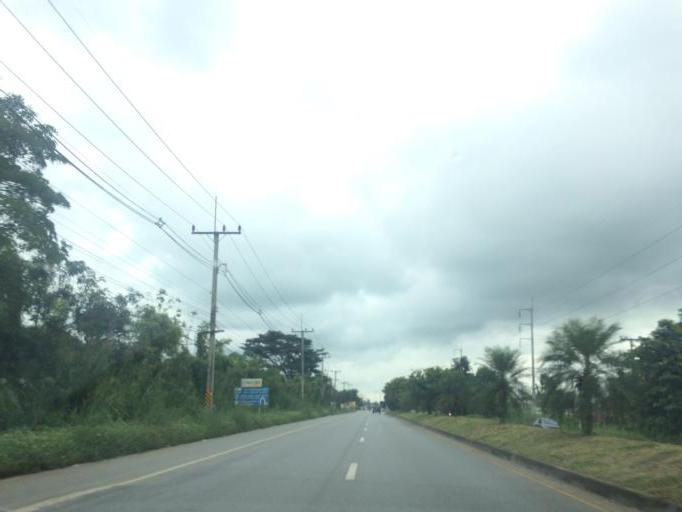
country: TH
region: Chiang Rai
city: Mae Chan
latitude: 20.0680
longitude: 99.8756
